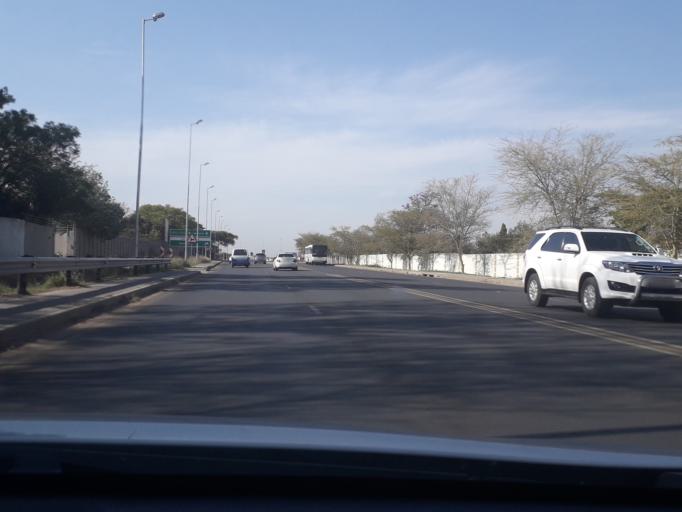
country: ZA
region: Gauteng
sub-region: City of Johannesburg Metropolitan Municipality
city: Diepsloot
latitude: -25.9909
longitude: 27.9838
